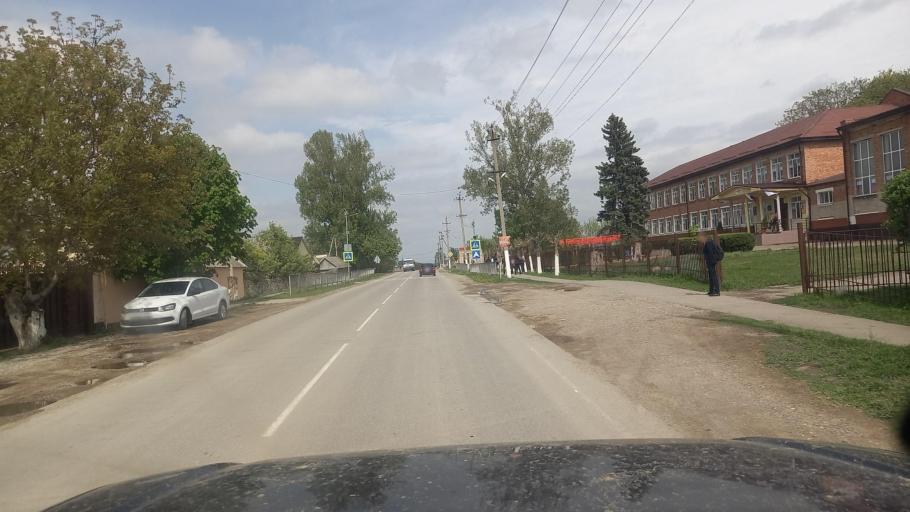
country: RU
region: Kabardino-Balkariya
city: Sarmakovo
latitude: 43.7350
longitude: 43.1773
